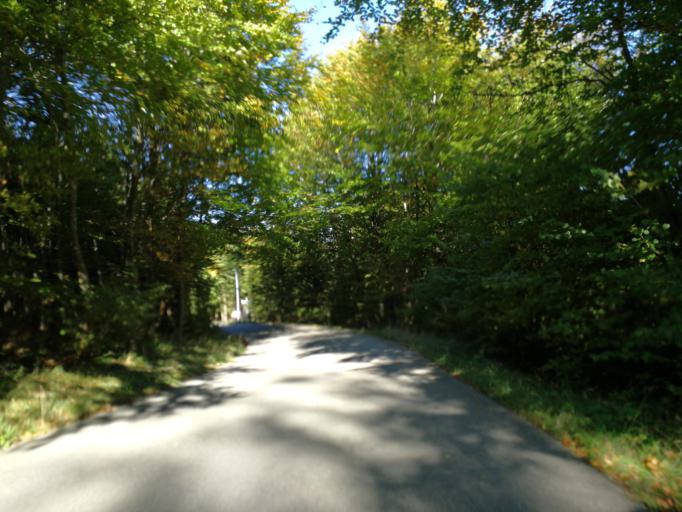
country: CH
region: Zurich
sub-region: Bezirk Uster
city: Aesch
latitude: 47.3139
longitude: 8.6586
